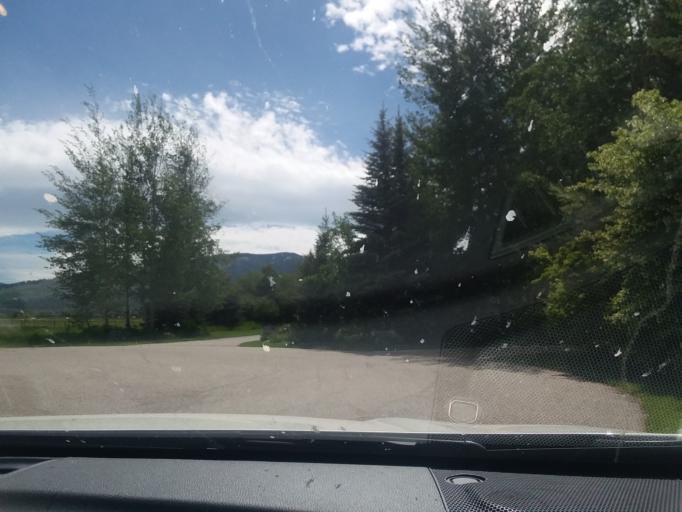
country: US
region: Wyoming
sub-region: Teton County
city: Wilson
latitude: 43.5033
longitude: -110.8529
